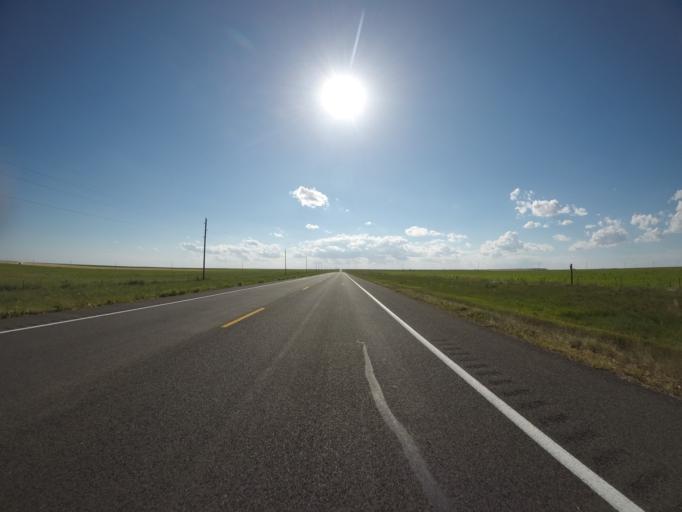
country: US
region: Colorado
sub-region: Morgan County
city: Fort Morgan
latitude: 40.6106
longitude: -103.7474
